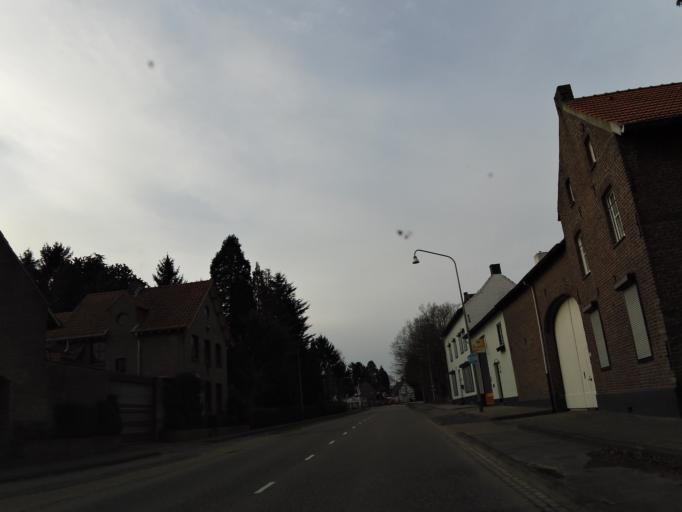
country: NL
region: Limburg
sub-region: Gemeente Schinnen
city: Amstenrade
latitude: 50.9354
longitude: 5.9161
